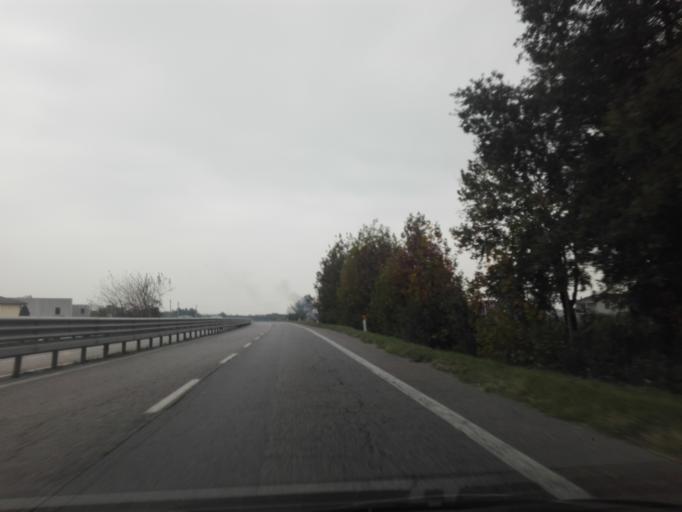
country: IT
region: Veneto
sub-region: Provincia di Verona
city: Isola Rizza
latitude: 45.2805
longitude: 11.2068
